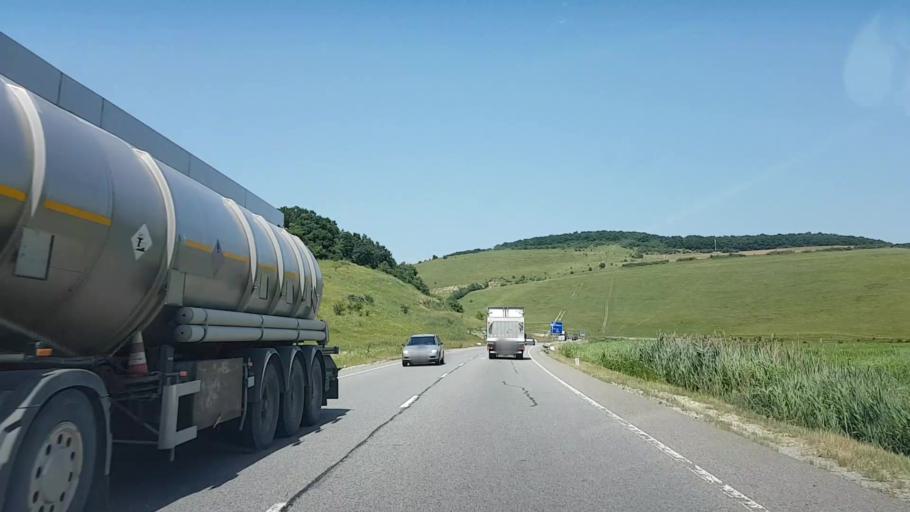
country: RO
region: Cluj
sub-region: Comuna Apahida
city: Dezmir
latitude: 46.7401
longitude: 23.7090
